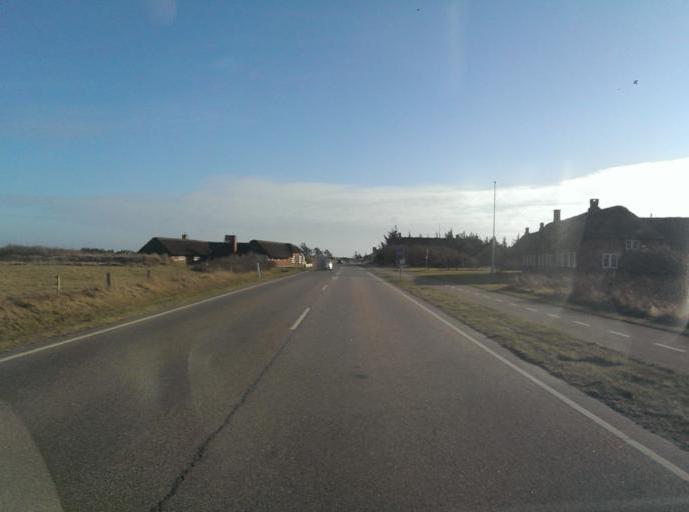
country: DK
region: Central Jutland
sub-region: Ringkobing-Skjern Kommune
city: Hvide Sande
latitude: 56.0490
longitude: 8.1193
